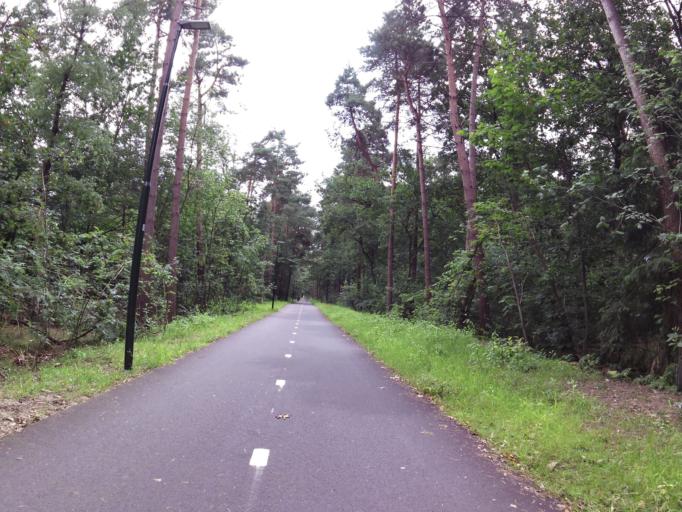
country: NL
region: North Brabant
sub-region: Gemeente Valkenswaard
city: Valkenswaard
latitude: 51.3688
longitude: 5.4614
